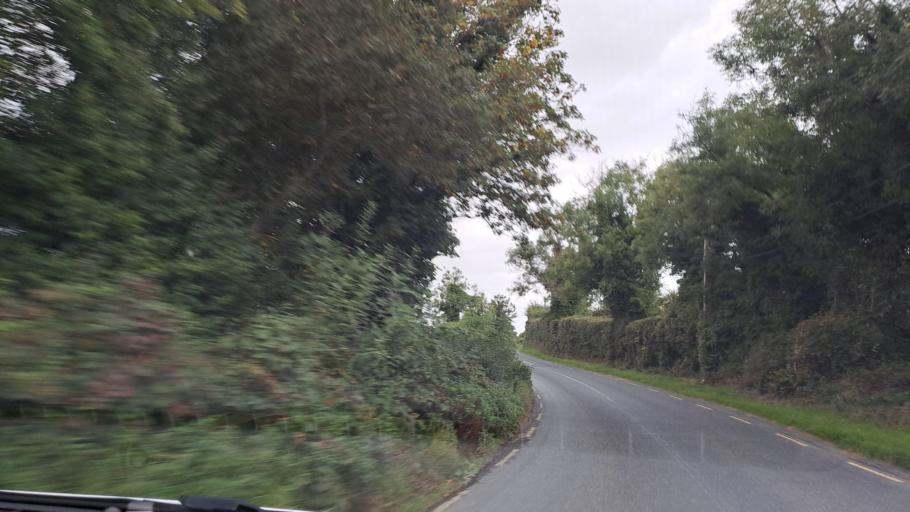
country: IE
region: Ulster
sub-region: An Cabhan
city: Bailieborough
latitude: 54.0039
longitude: -6.9065
